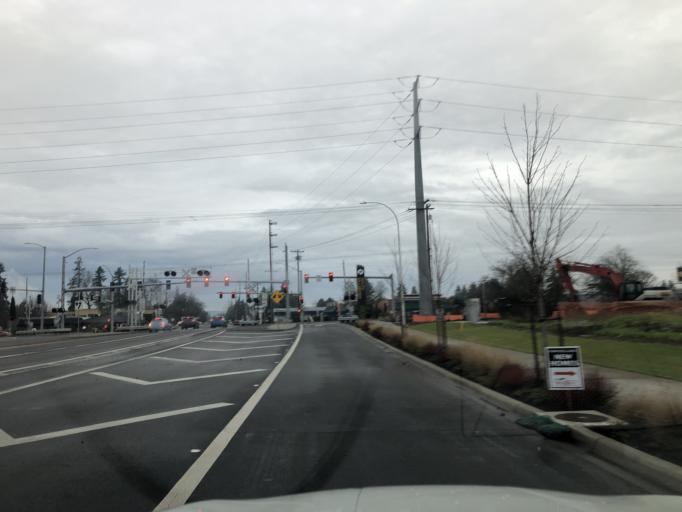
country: US
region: Oregon
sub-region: Washington County
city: Aloha
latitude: 45.4966
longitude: -122.9022
